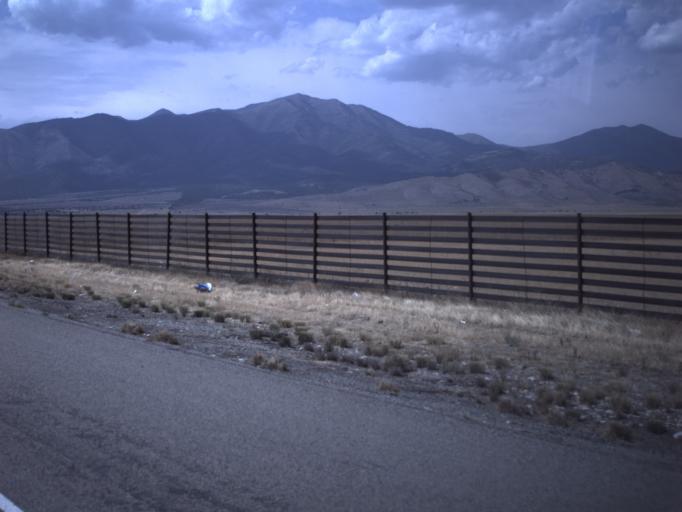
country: US
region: Utah
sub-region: Utah County
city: Eagle Mountain
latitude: 40.3630
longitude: -112.0441
